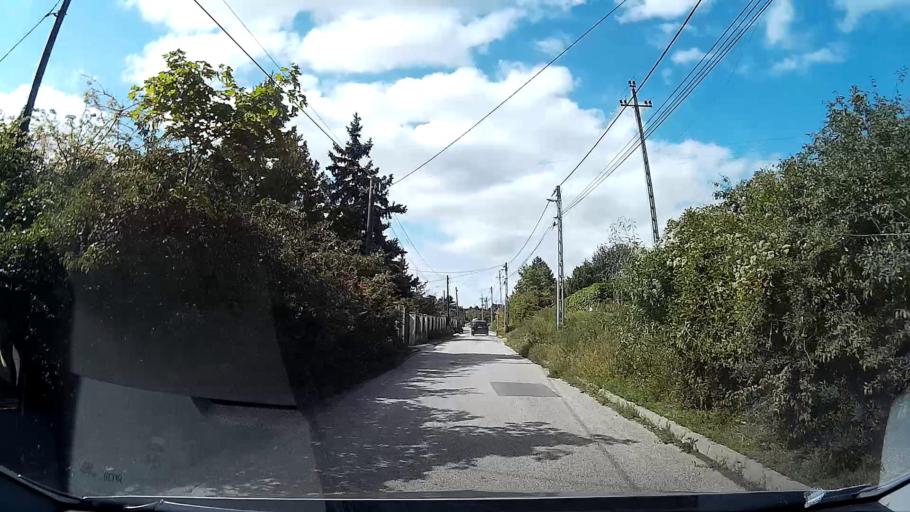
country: HU
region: Pest
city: Szentendre
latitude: 47.6913
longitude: 19.0702
